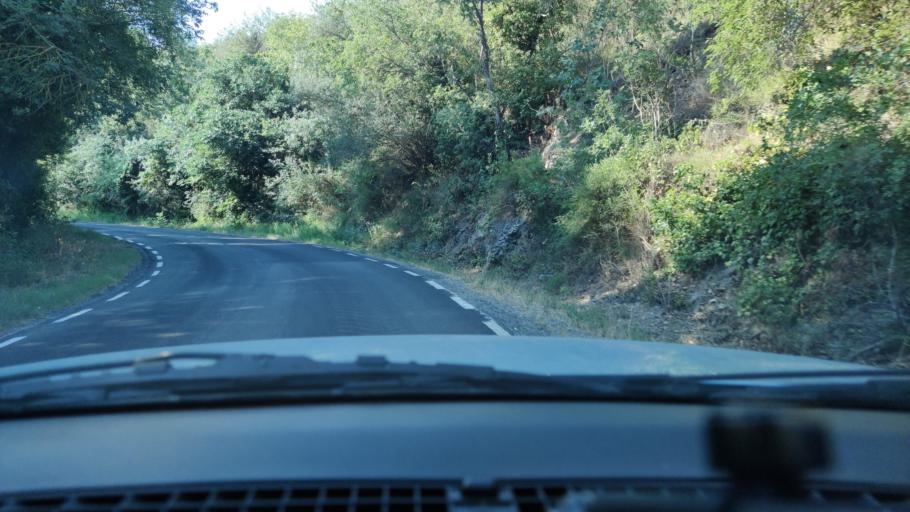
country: ES
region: Catalonia
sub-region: Provincia de Lleida
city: Camarasa
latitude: 41.8686
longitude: 0.8640
